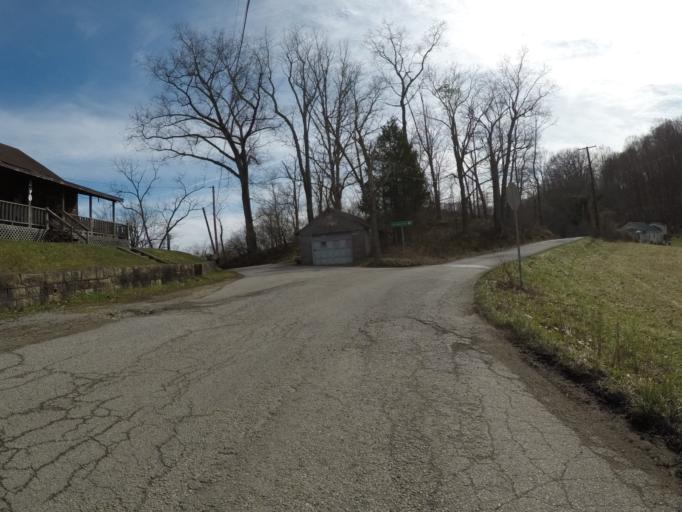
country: US
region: West Virginia
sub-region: Wayne County
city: Lavalette
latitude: 38.3460
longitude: -82.5060
